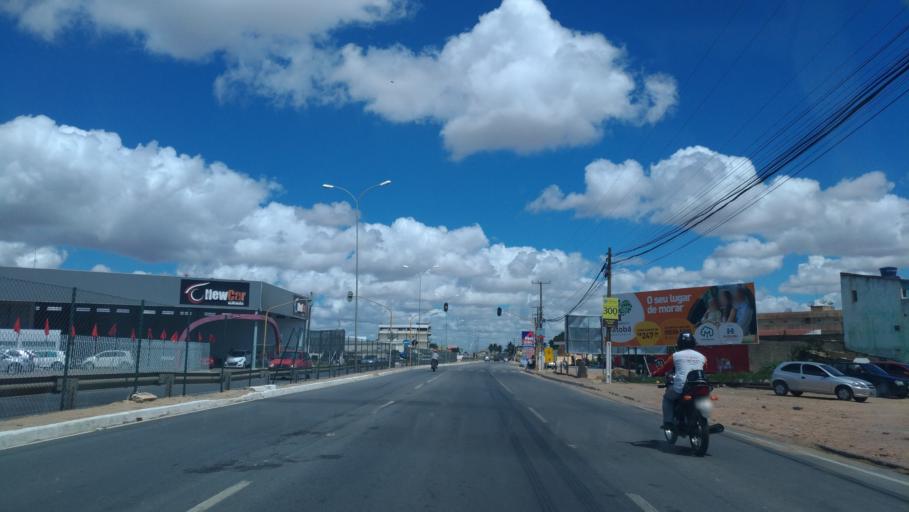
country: BR
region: Alagoas
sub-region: Arapiraca
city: Arapiraca
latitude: -9.7278
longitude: -36.6684
